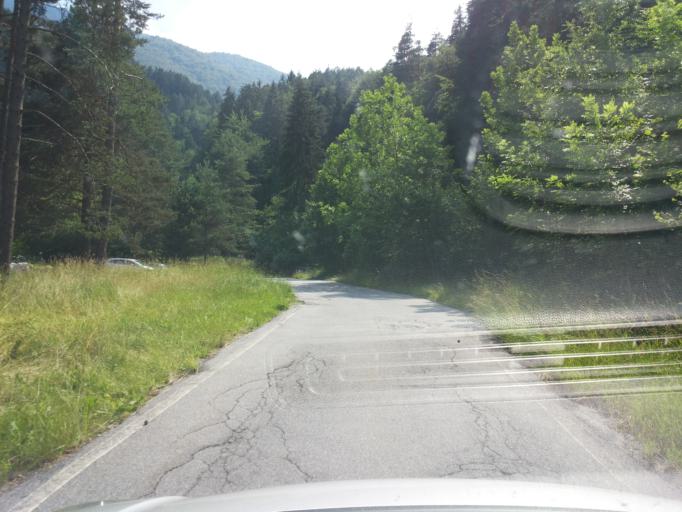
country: IT
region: Piedmont
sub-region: Provincia Verbano-Cusio-Ossola
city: Malesco
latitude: 46.1262
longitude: 8.4935
